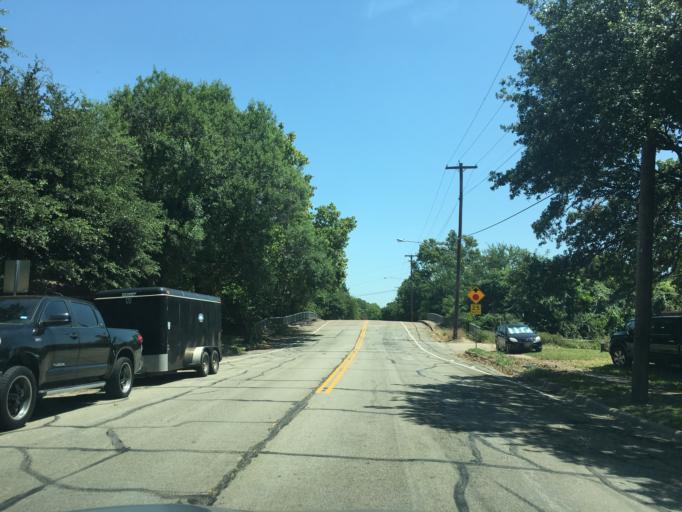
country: US
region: Texas
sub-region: Dallas County
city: Highland Park
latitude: 32.8488
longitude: -96.7423
